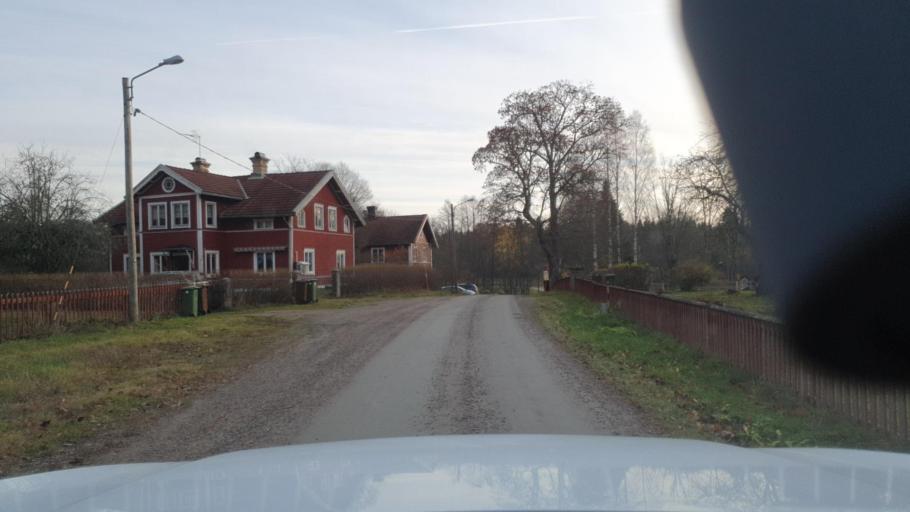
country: SE
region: Uppsala
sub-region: Tierps Kommun
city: Karlholmsbruk
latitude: 60.4835
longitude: 17.5156
